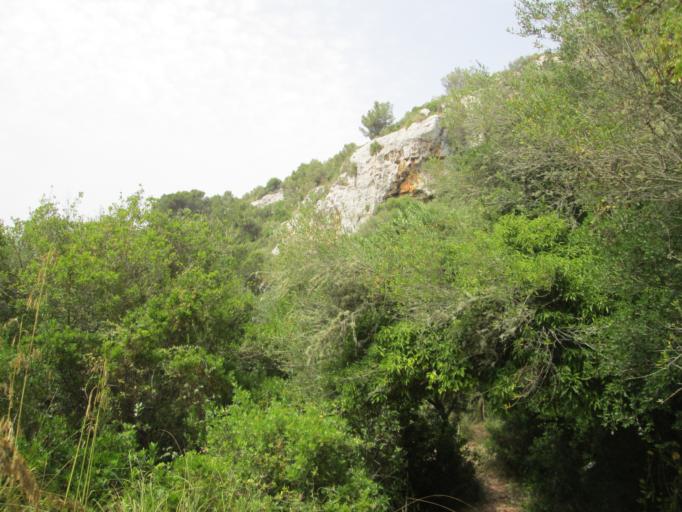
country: ES
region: Balearic Islands
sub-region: Illes Balears
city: Es Migjorn Gran
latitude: 39.9339
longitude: 4.0387
